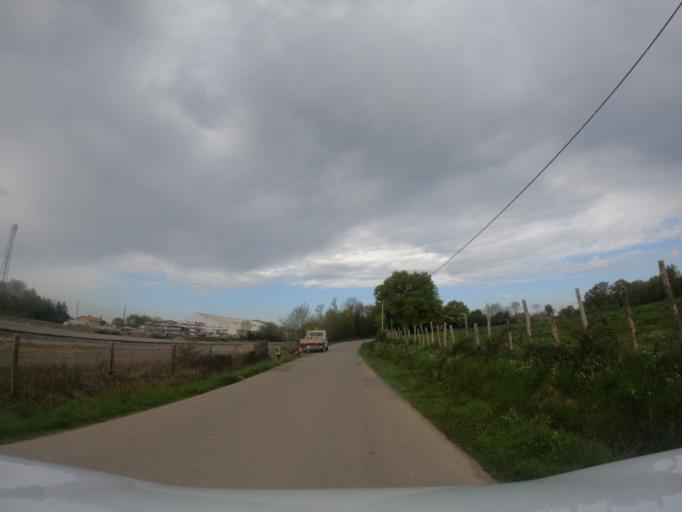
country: FR
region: Pays de la Loire
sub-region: Departement de la Vendee
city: Le Champ-Saint-Pere
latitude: 46.5139
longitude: -1.3438
